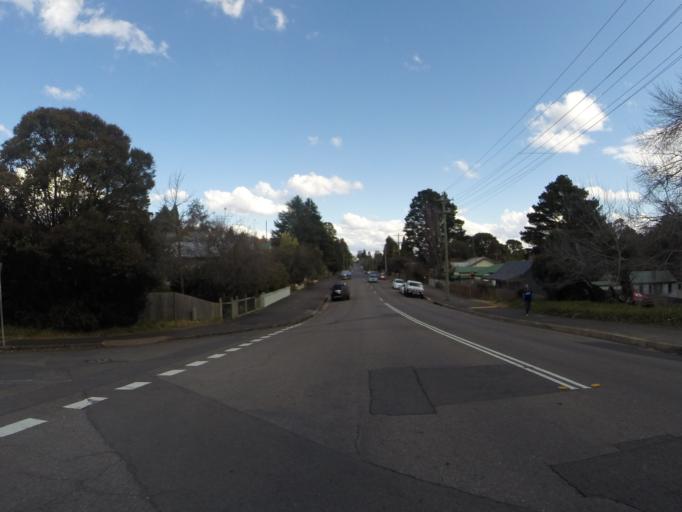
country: AU
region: New South Wales
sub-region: Blue Mountains Municipality
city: Katoomba
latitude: -33.7210
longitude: 150.3102
